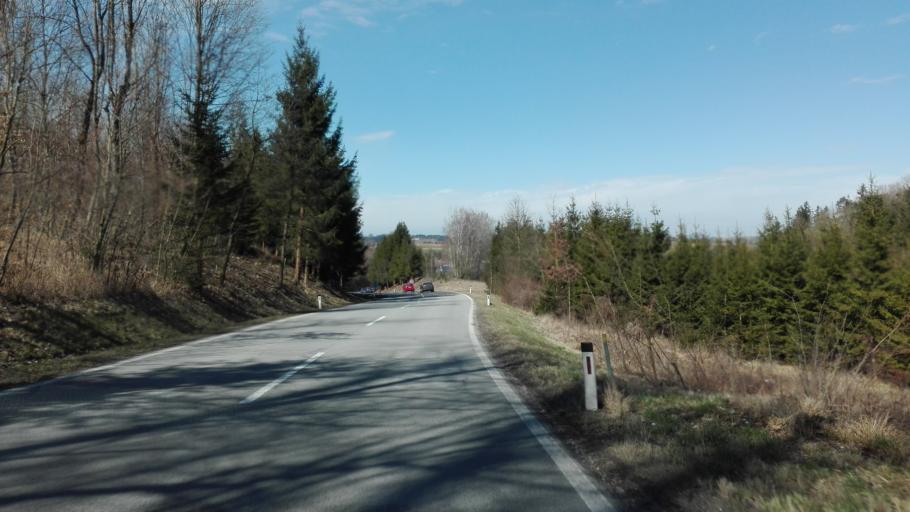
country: AT
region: Upper Austria
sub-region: Wels-Land
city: Gunskirchen
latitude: 48.1850
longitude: 13.9615
